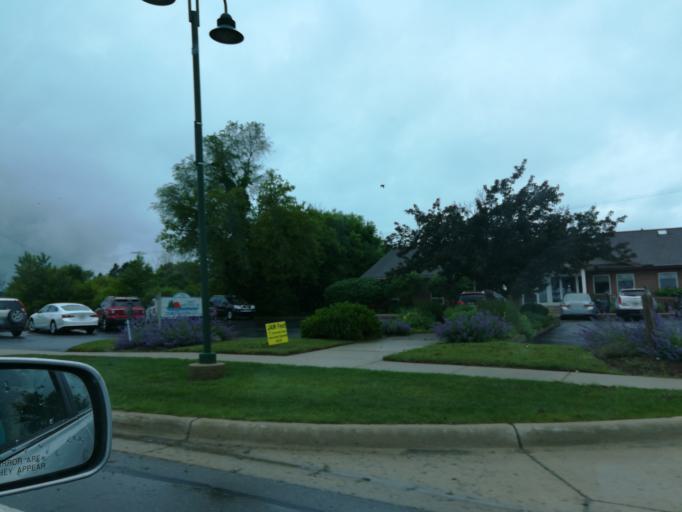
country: US
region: Michigan
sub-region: Iosco County
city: Tawas City
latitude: 44.2670
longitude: -83.5186
